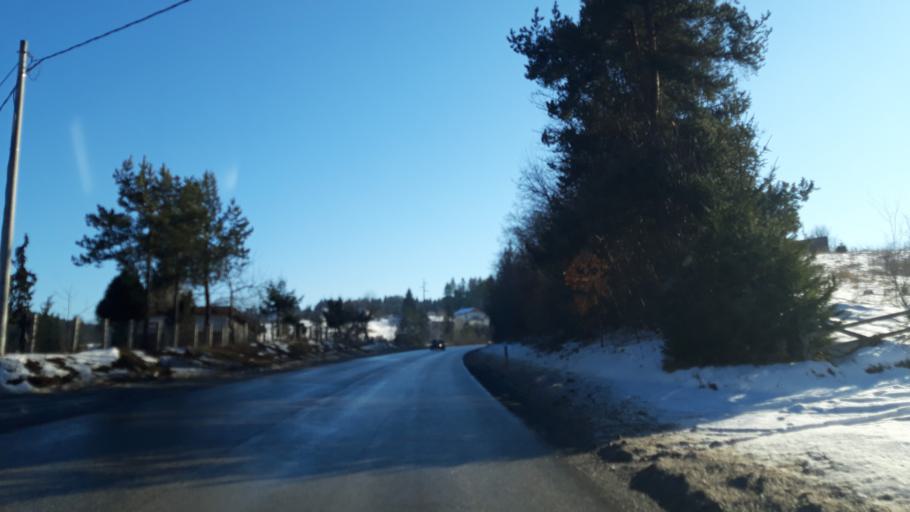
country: BA
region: Republika Srpska
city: Pale
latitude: 43.8366
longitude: 18.5572
